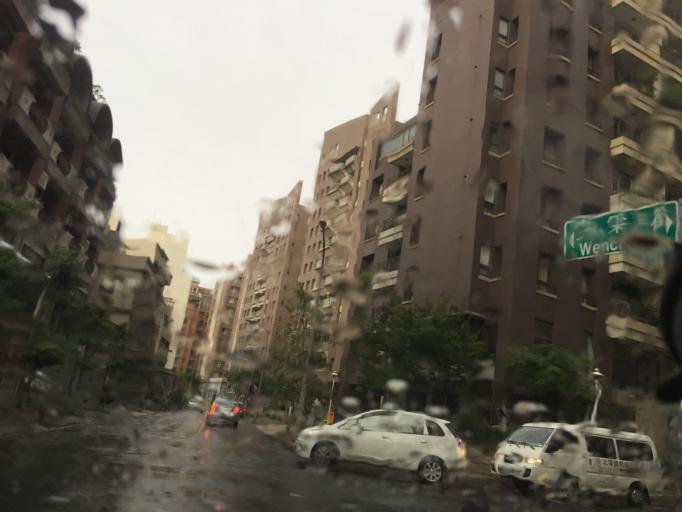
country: TW
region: Taiwan
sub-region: Hsinchu
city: Zhubei
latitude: 24.8331
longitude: 121.0180
